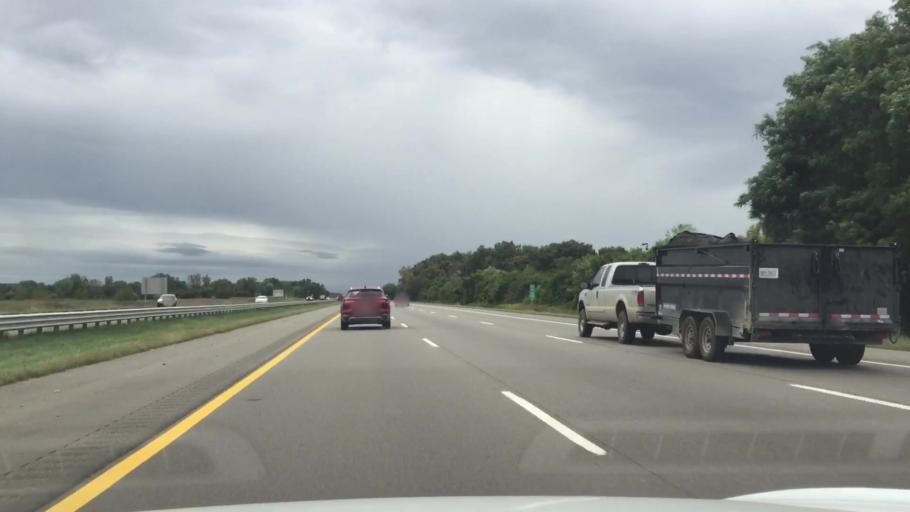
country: US
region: Michigan
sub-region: Macomb County
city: New Haven
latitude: 42.6592
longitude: -82.8317
